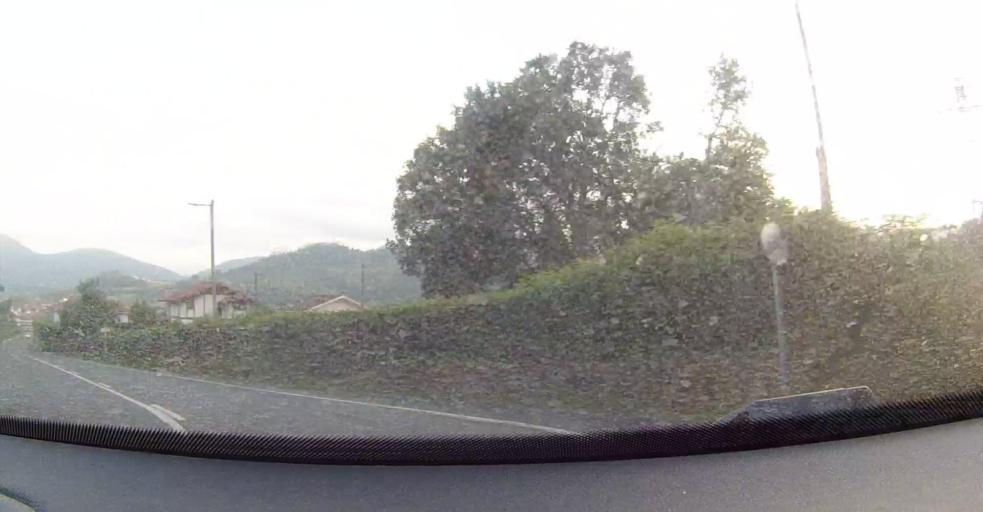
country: ES
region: Basque Country
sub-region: Bizkaia
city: Sopuerta
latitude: 43.2835
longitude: -3.1615
